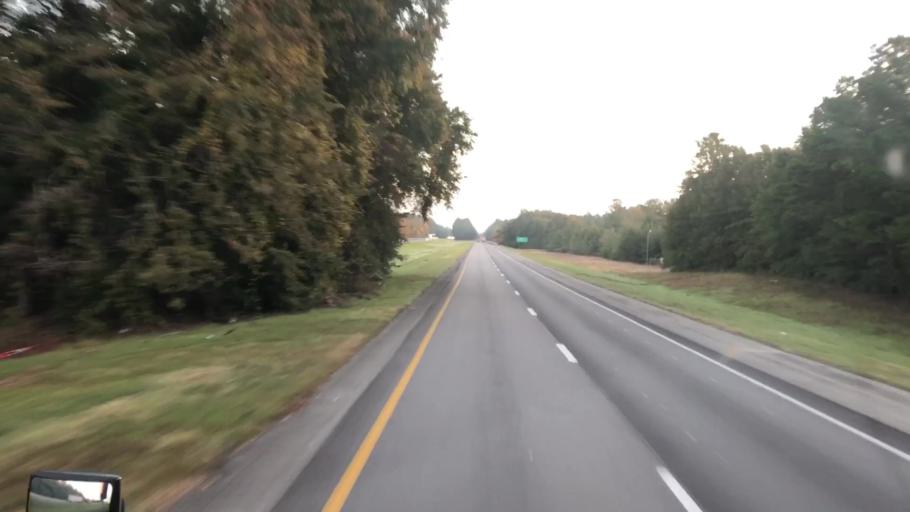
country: US
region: South Carolina
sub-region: Orangeburg County
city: Holly Hill
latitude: 33.5271
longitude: -80.4259
